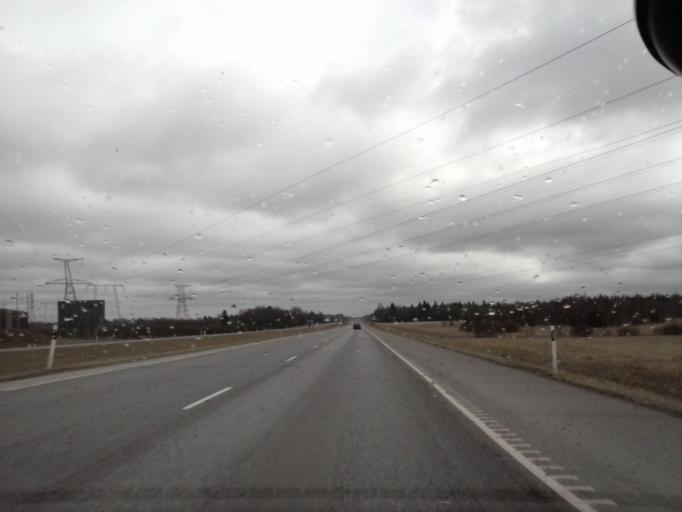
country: EE
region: Harju
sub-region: Rae vald
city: Vaida
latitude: 59.2755
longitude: 24.9847
